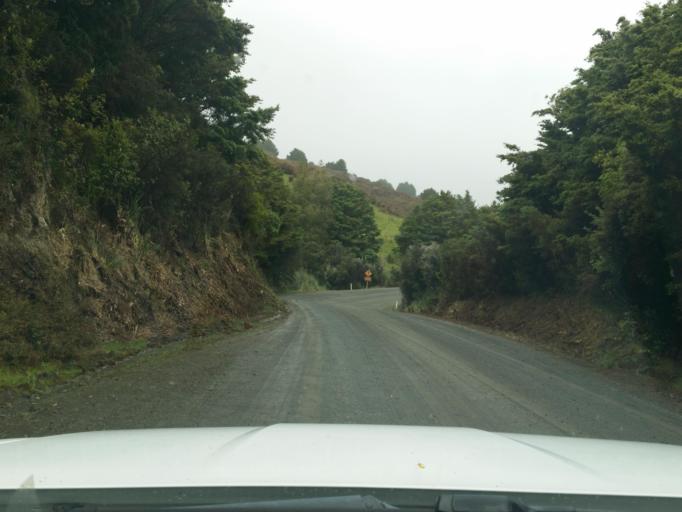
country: NZ
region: Northland
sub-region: Kaipara District
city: Dargaville
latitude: -35.7352
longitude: 173.9087
